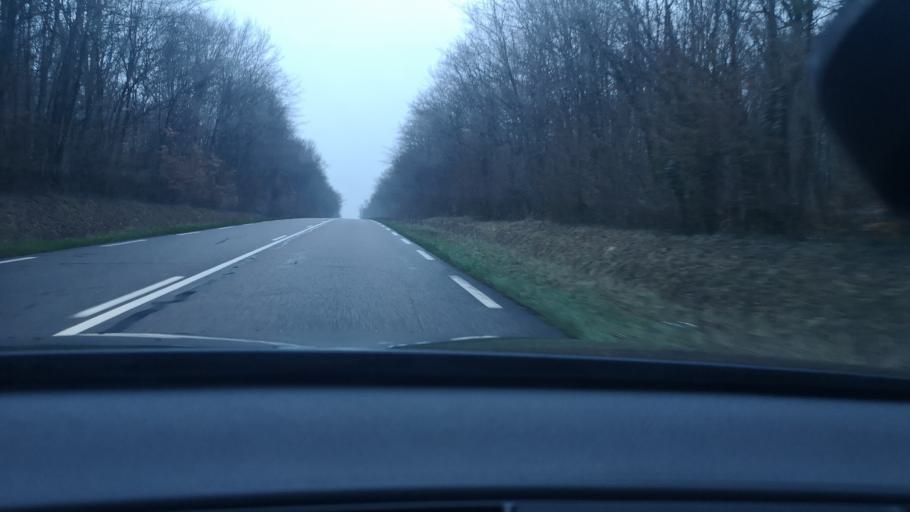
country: FR
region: Bourgogne
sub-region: Departement de la Cote-d'Or
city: Aiserey
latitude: 47.0985
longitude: 5.1036
